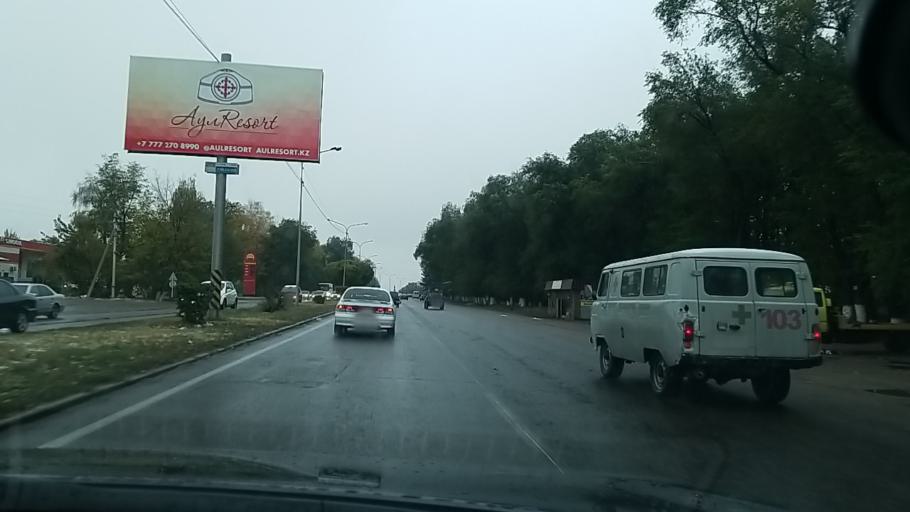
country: KZ
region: Almaty Oblysy
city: Burunday
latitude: 43.2142
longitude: 76.6856
